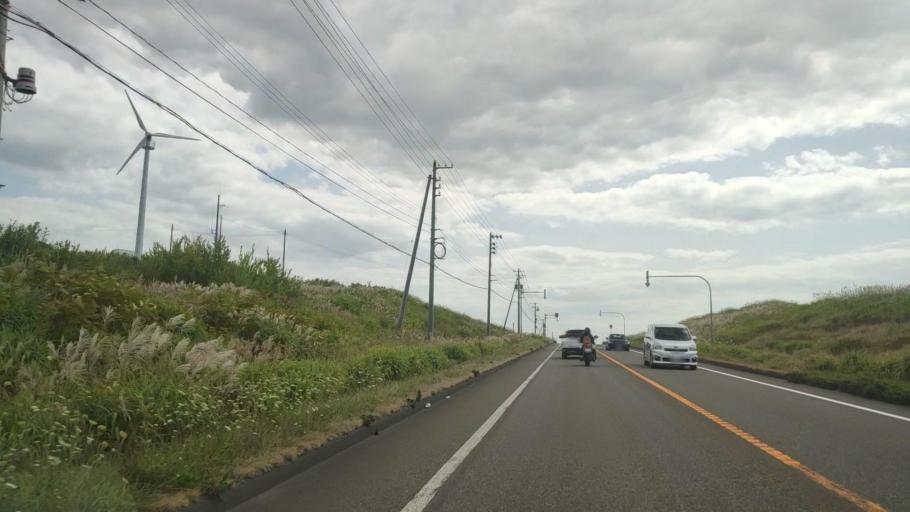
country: JP
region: Hokkaido
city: Rumoi
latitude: 44.5221
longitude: 141.7655
